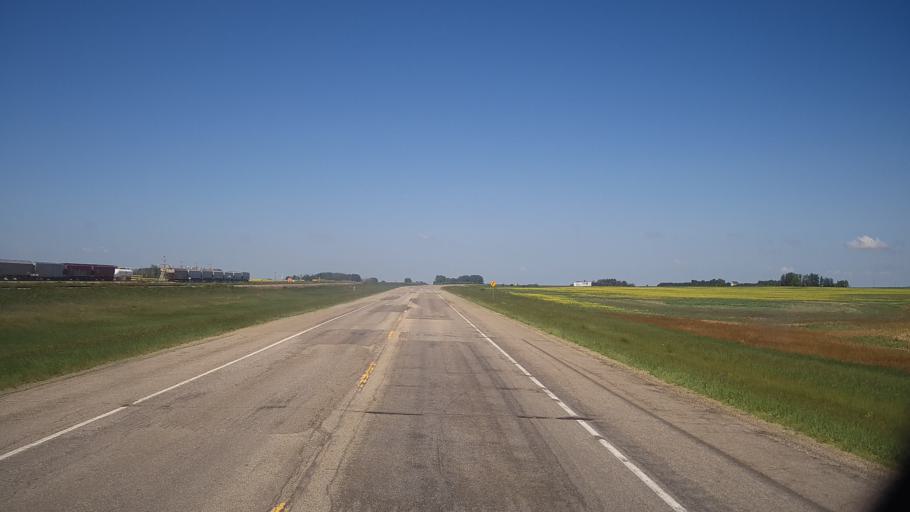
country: CA
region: Saskatchewan
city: Saskatoon
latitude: 51.9938
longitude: -106.0917
